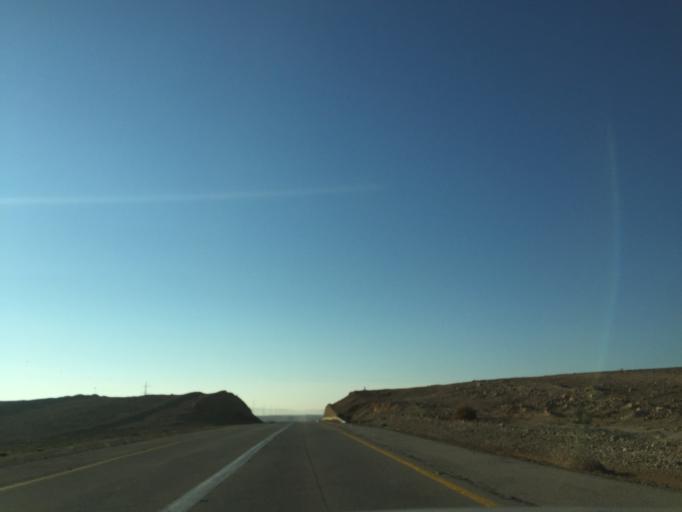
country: IL
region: Southern District
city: Mitzpe Ramon
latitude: 30.4618
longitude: 34.9346
